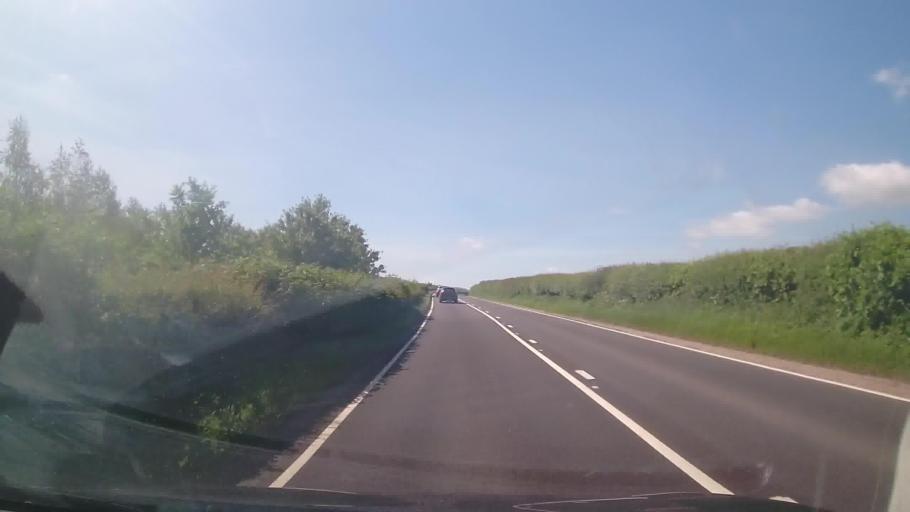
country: GB
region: England
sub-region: Shropshire
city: Craven Arms
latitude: 52.4871
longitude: -2.8158
